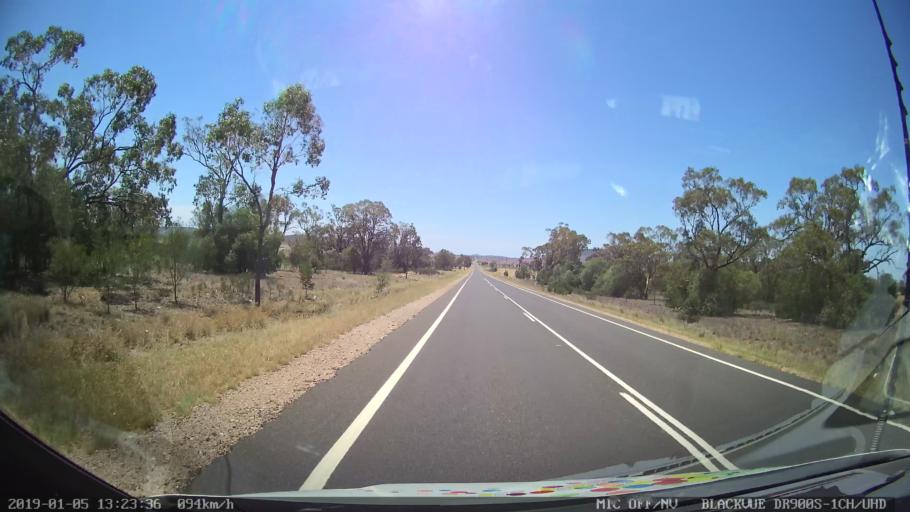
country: AU
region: New South Wales
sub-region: Gunnedah
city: Gunnedah
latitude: -31.0767
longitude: 149.9772
